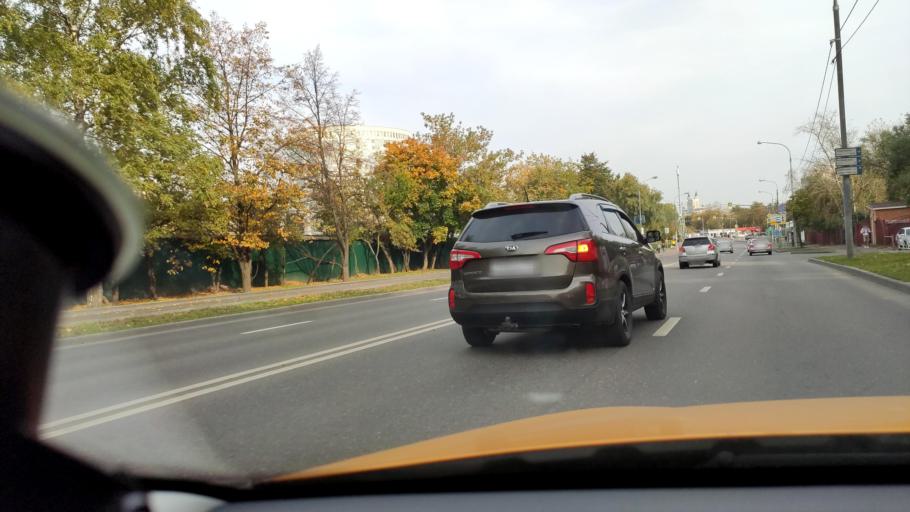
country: RU
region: Moscow
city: Davydkovo
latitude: 55.7262
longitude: 37.4447
